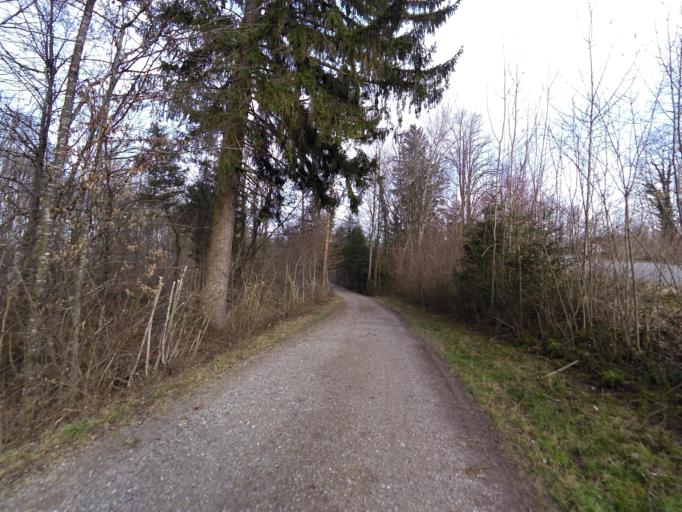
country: CH
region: Thurgau
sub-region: Frauenfeld District
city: Pfyn
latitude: 47.5859
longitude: 8.9357
